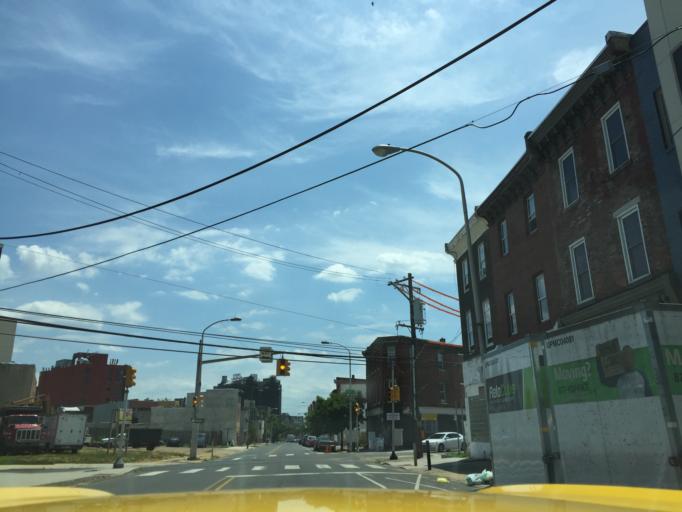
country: US
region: Pennsylvania
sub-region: Philadelphia County
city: Philadelphia
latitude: 39.9695
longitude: -75.1637
